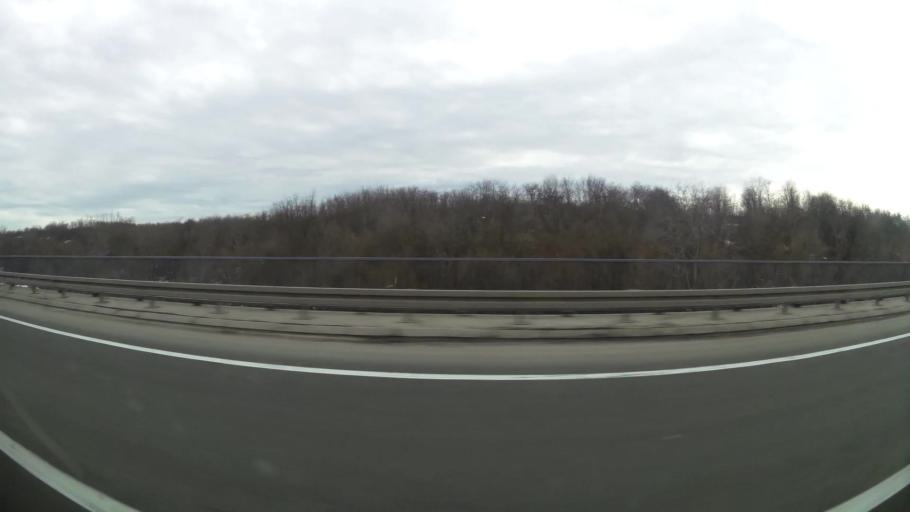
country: RS
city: Ostruznica
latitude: 44.7177
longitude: 20.3606
